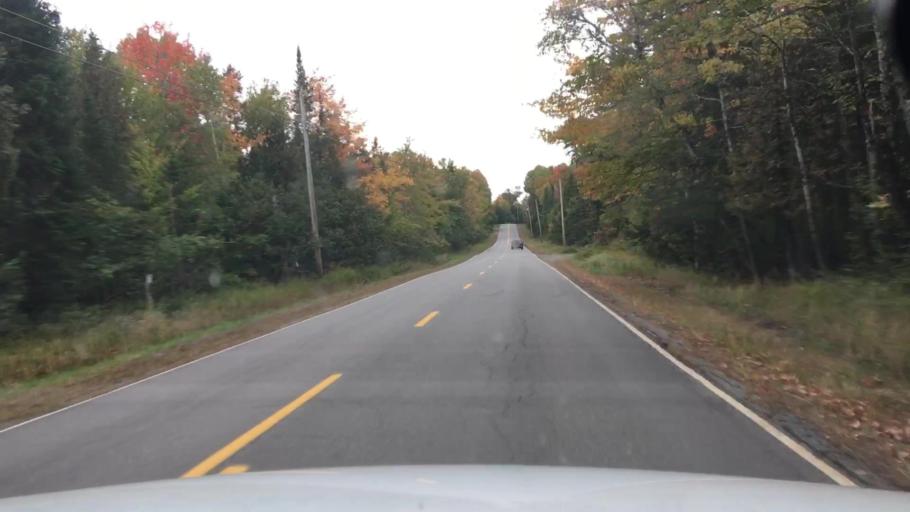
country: US
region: Maine
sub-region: Penobscot County
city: Hudson
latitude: 44.9847
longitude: -68.7836
